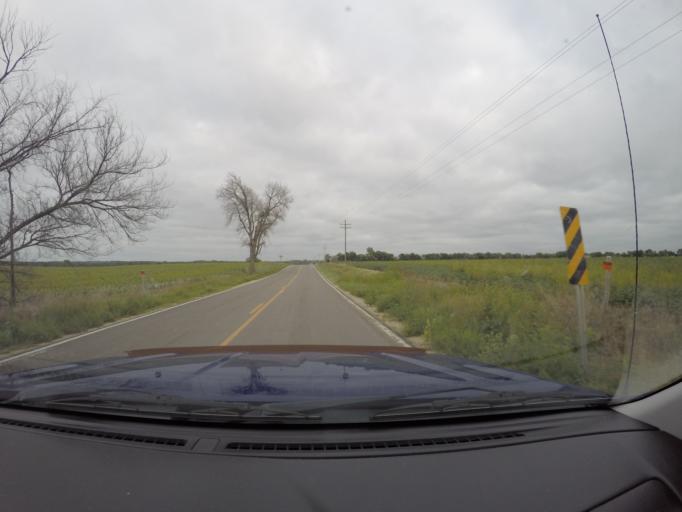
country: US
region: Kansas
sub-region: Dickinson County
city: Herington
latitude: 38.7979
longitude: -96.9540
